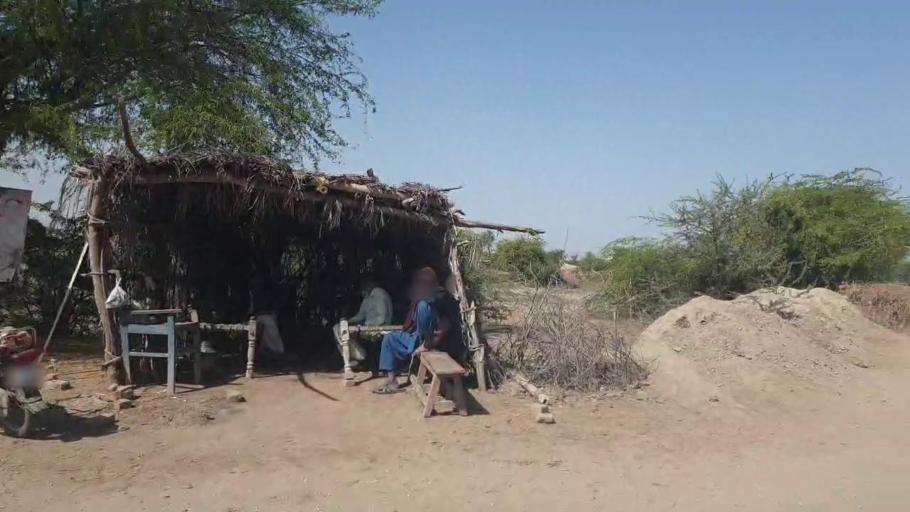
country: PK
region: Sindh
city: Kunri
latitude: 25.2782
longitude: 69.6306
